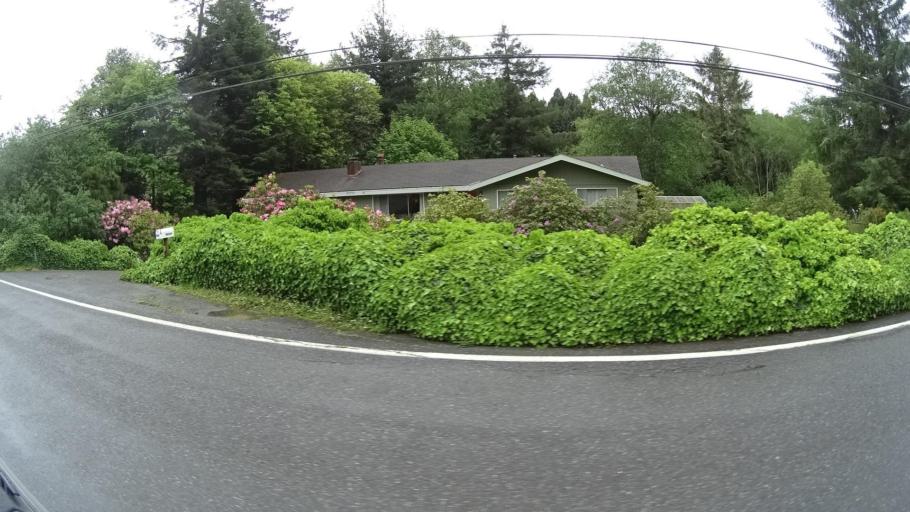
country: US
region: California
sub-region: Humboldt County
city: Bayside
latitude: 40.8337
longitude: -124.0452
